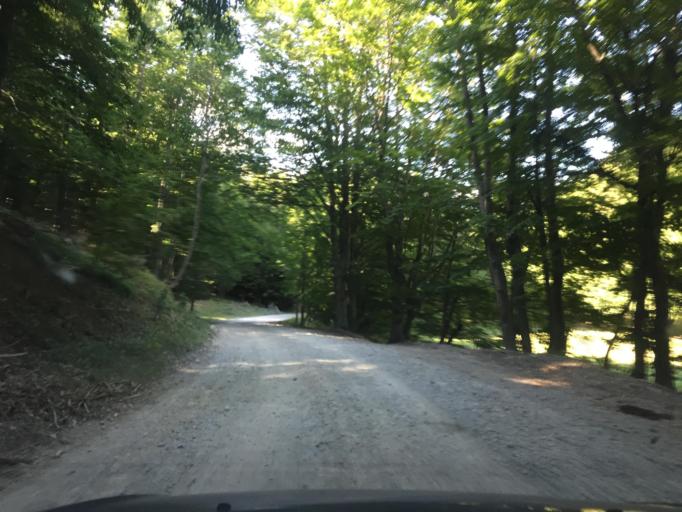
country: HR
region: Primorsko-Goranska
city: Klana
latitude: 45.4715
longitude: 14.4010
